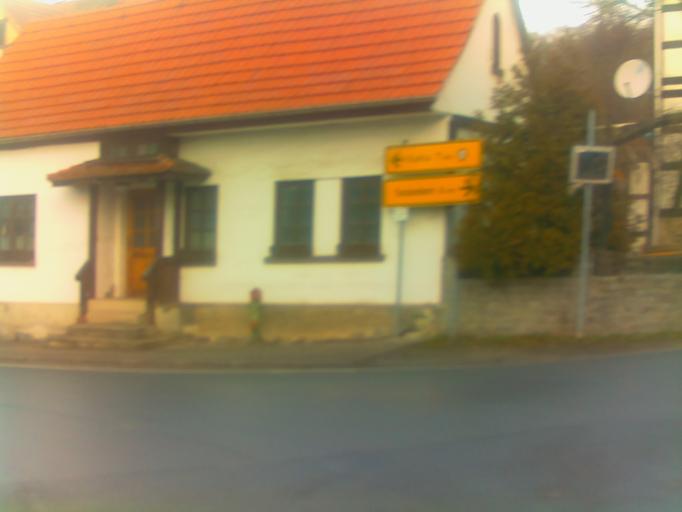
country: DE
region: Thuringia
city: Hummelshain
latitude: 50.7670
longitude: 11.6299
